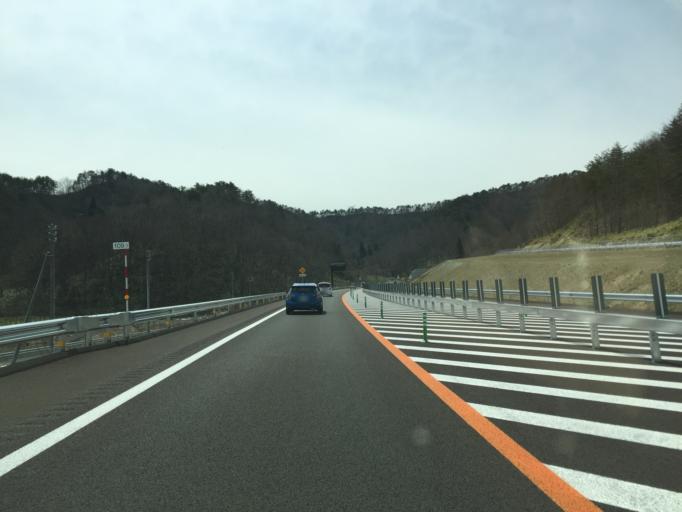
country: JP
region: Yamagata
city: Kaminoyama
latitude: 38.1168
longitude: 140.2476
